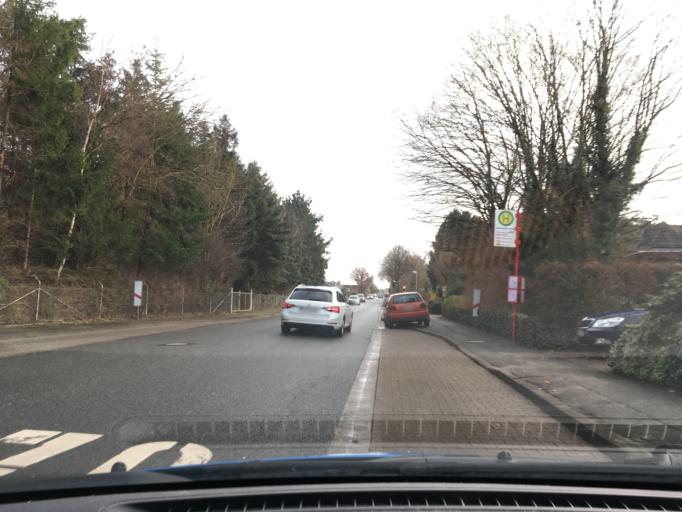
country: DE
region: Lower Saxony
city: Adendorf
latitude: 53.2640
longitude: 10.4634
